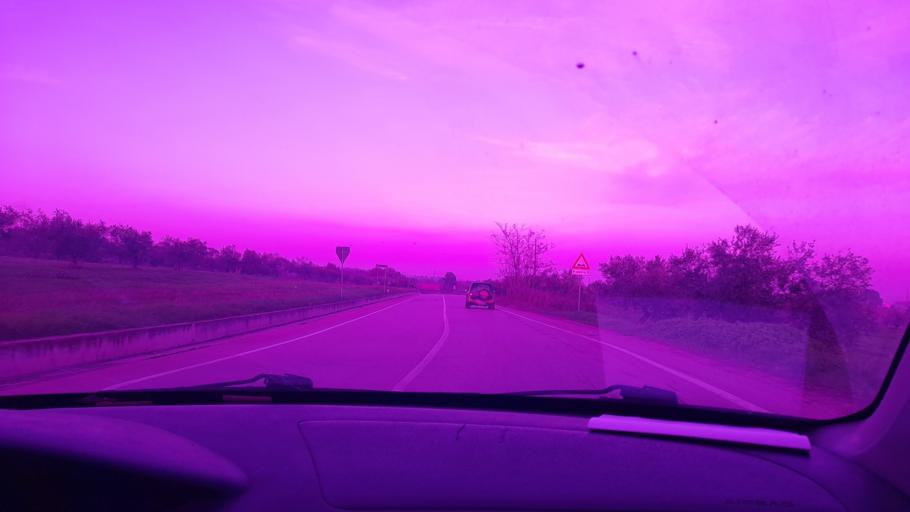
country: IT
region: Abruzzo
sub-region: Provincia di Pescara
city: Cappelle sul Tavo
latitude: 42.4880
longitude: 14.0799
